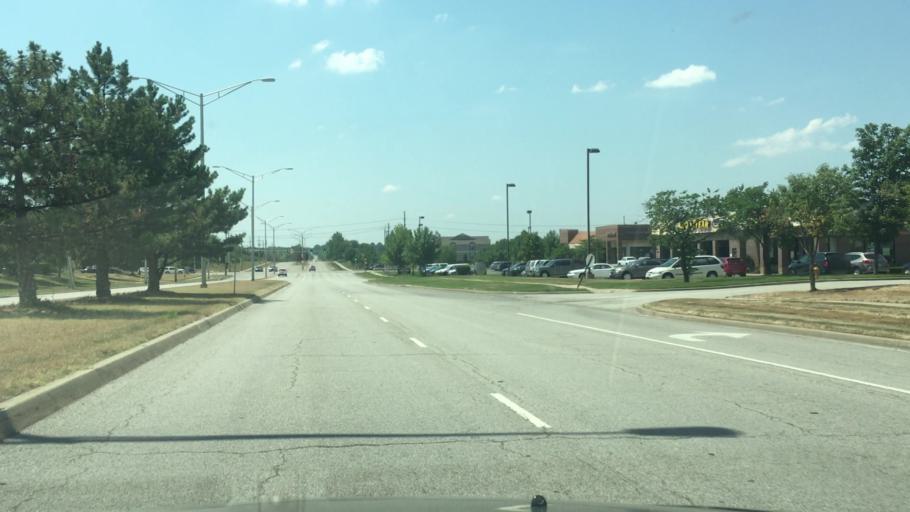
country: US
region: Kansas
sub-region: Johnson County
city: Lenexa
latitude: 38.8859
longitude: -94.7238
